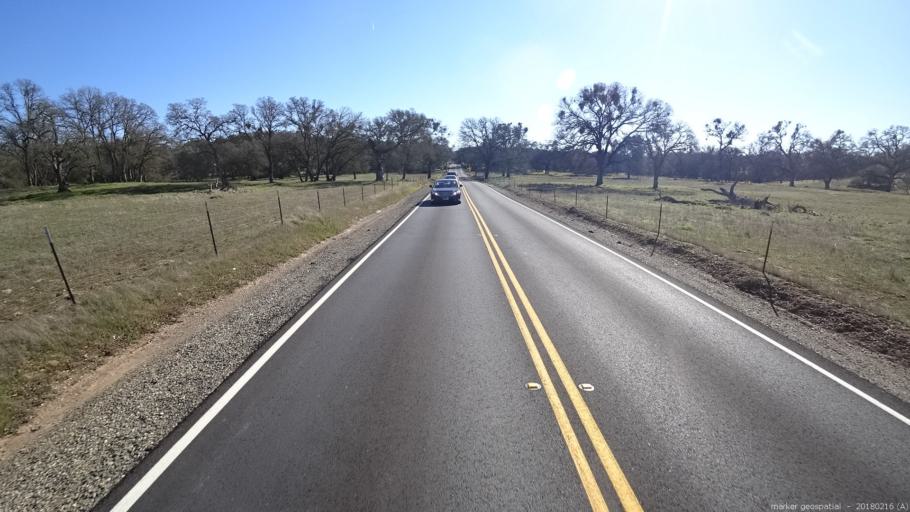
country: US
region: California
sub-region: Sacramento County
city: Rancho Murieta
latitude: 38.5349
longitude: -121.1040
